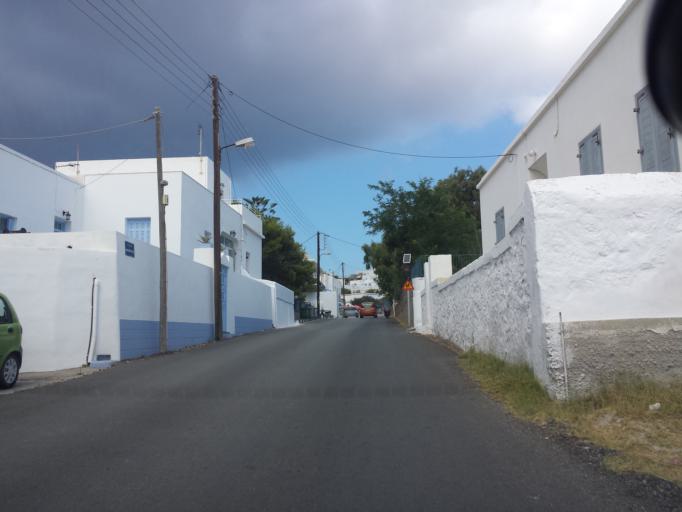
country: GR
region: South Aegean
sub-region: Nomos Kykladon
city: Milos
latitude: 36.7434
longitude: 24.4267
